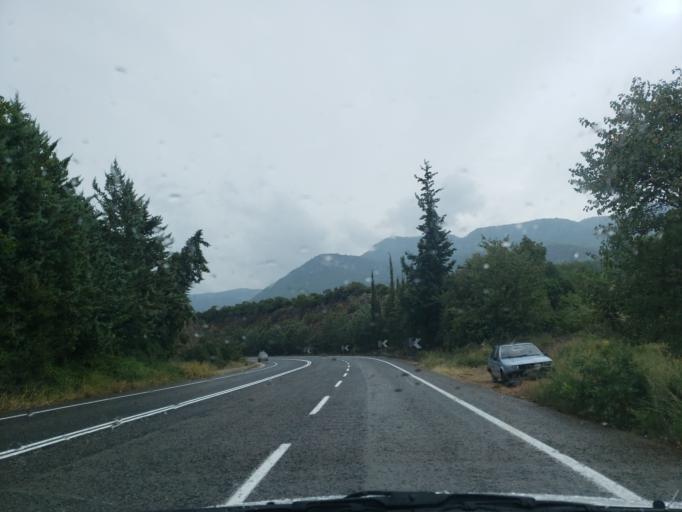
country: GR
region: Central Greece
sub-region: Nomos Fthiotidos
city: Anthili
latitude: 38.7908
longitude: 22.4752
